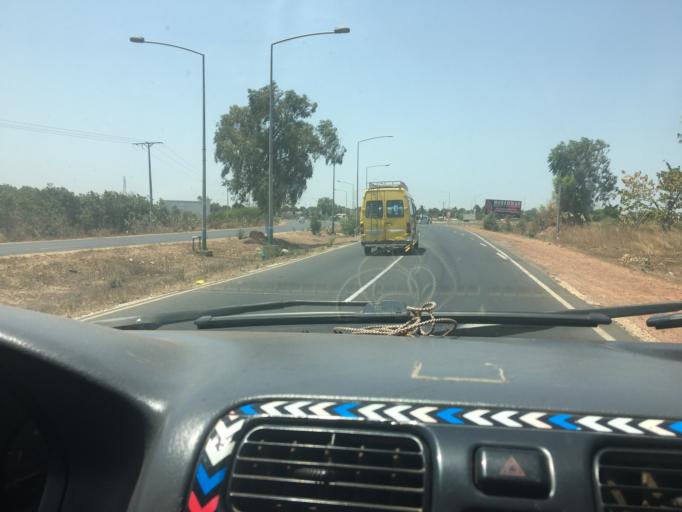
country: GM
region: Banjul
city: Bakau
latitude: 13.4654
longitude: -16.6554
